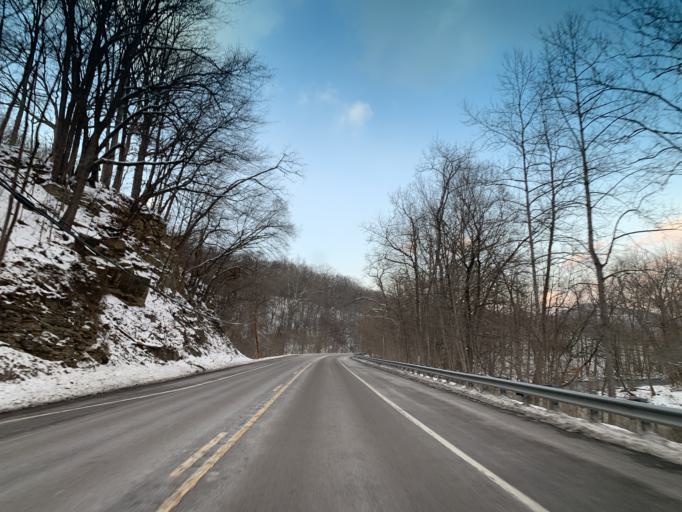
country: US
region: Maryland
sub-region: Allegany County
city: La Vale
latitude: 39.6763
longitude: -78.7917
